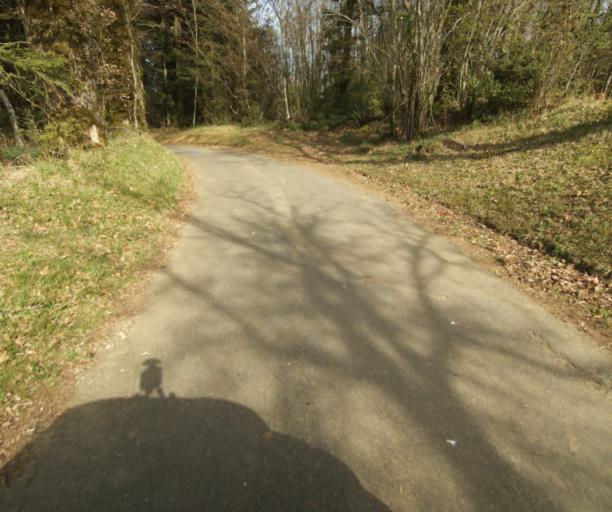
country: FR
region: Limousin
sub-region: Departement de la Correze
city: Naves
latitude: 45.3340
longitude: 1.7637
